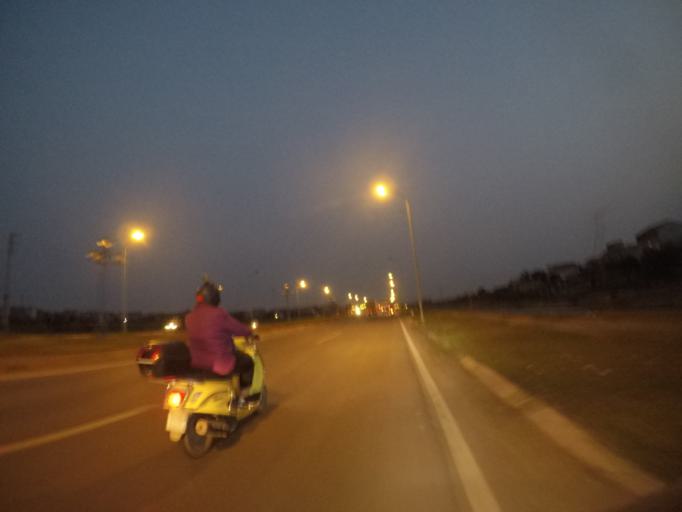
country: VN
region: Ha Noi
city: Me Linh
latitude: 21.1889
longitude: 105.7111
